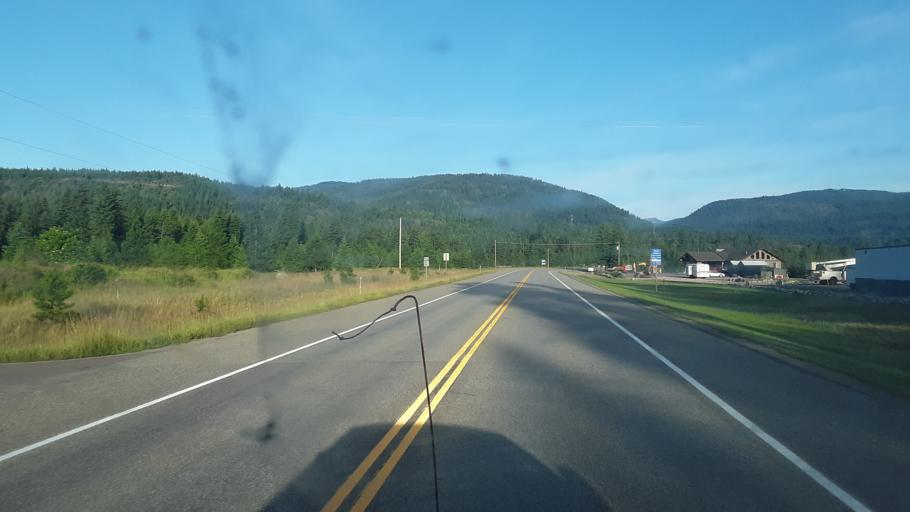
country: US
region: Montana
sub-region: Lincoln County
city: Libby
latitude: 48.4374
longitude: -115.8548
